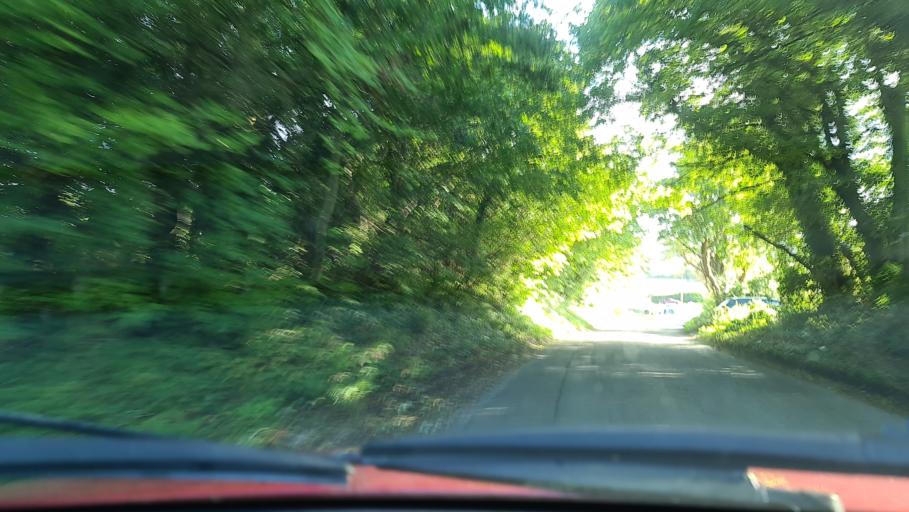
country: GB
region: England
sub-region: Buckinghamshire
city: Princes Risborough
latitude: 51.7079
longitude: -0.8392
